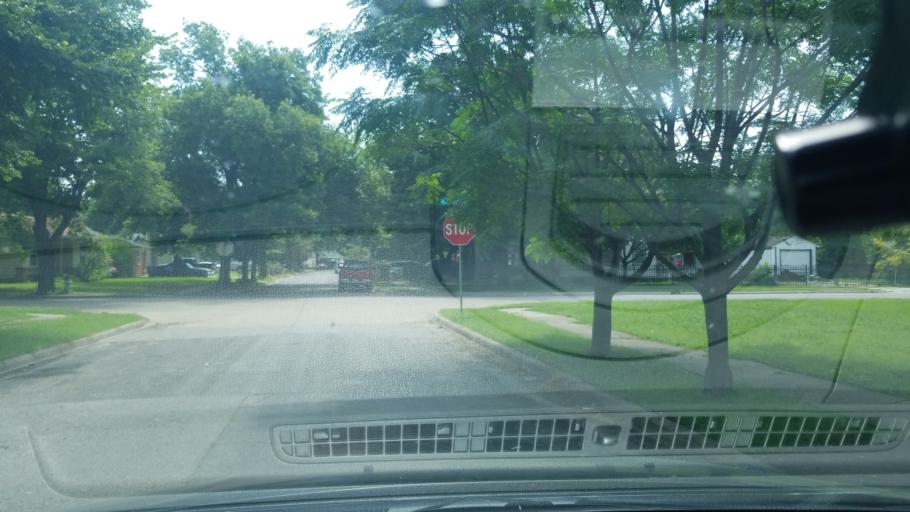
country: US
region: Texas
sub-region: Dallas County
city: Balch Springs
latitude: 32.7362
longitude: -96.6888
